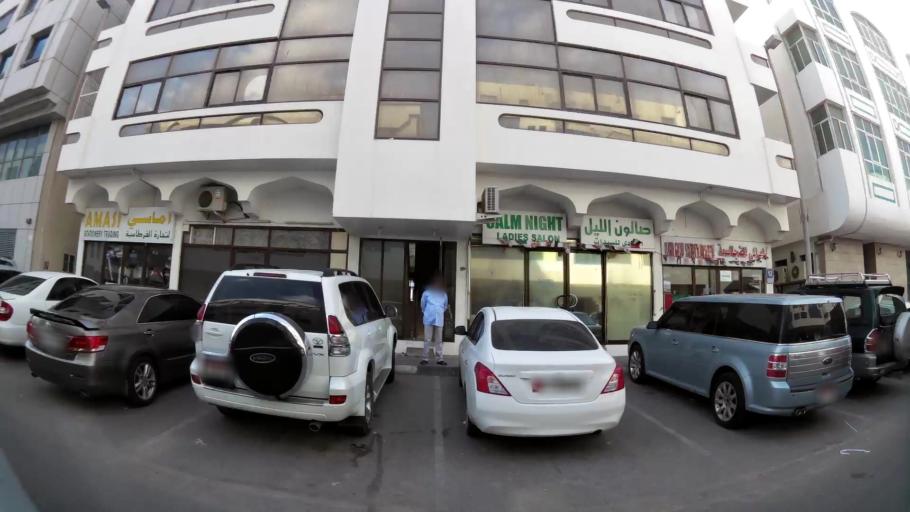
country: AE
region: Abu Dhabi
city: Abu Dhabi
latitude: 24.3299
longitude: 54.5336
